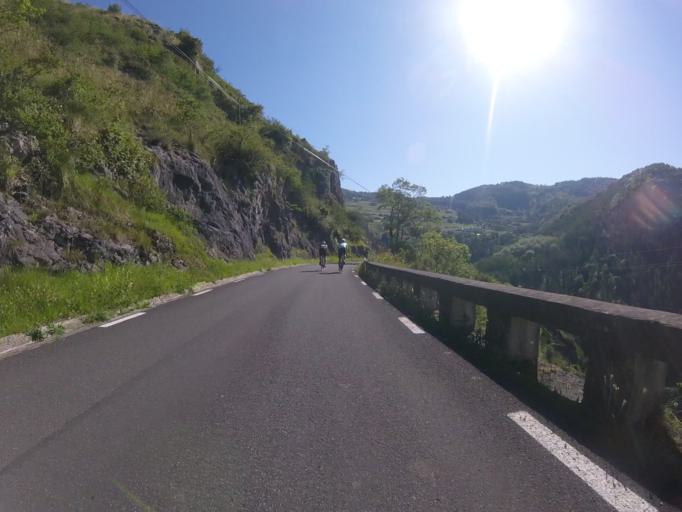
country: ES
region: Basque Country
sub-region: Provincia de Guipuzcoa
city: Beizama
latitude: 43.1326
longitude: -2.2098
